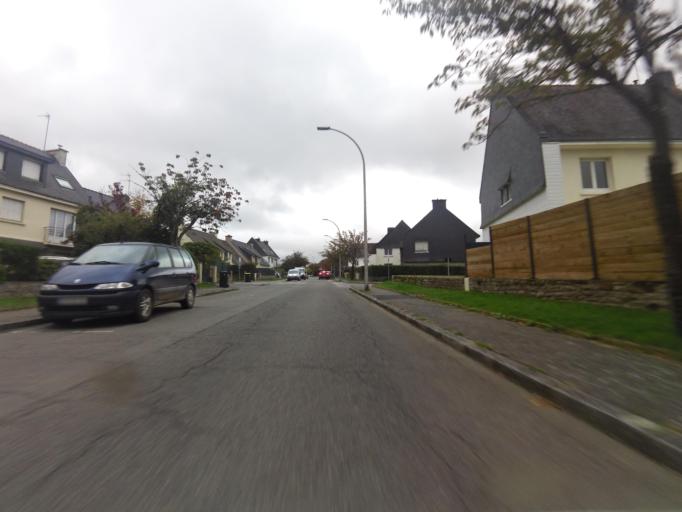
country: FR
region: Brittany
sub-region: Departement du Morbihan
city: Vannes
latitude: 47.6754
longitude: -2.7632
